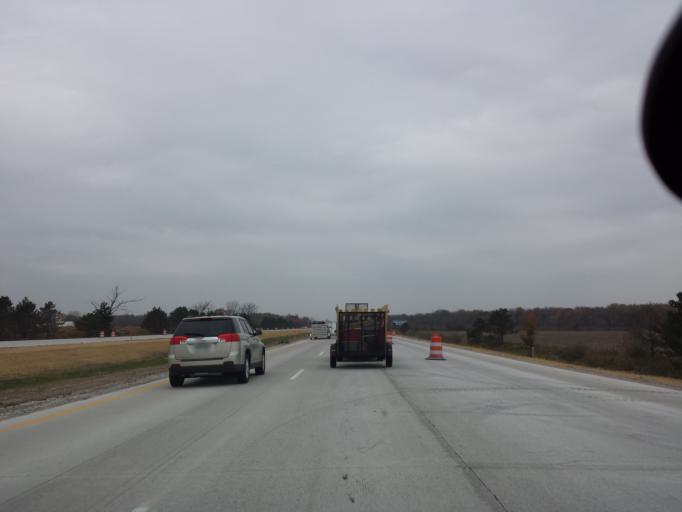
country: US
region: Michigan
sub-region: Bay County
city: Pinconning
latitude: 43.9003
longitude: -84.0199
